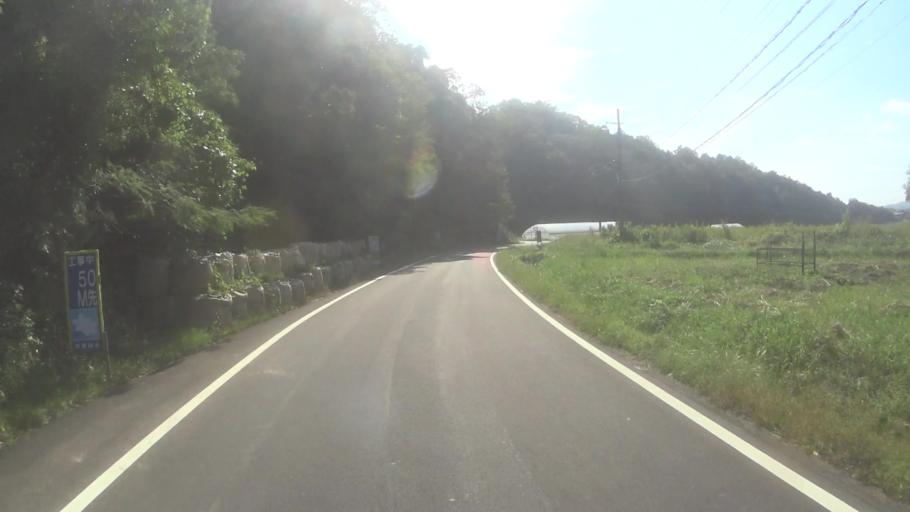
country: JP
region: Kyoto
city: Miyazu
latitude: 35.6818
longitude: 135.1106
